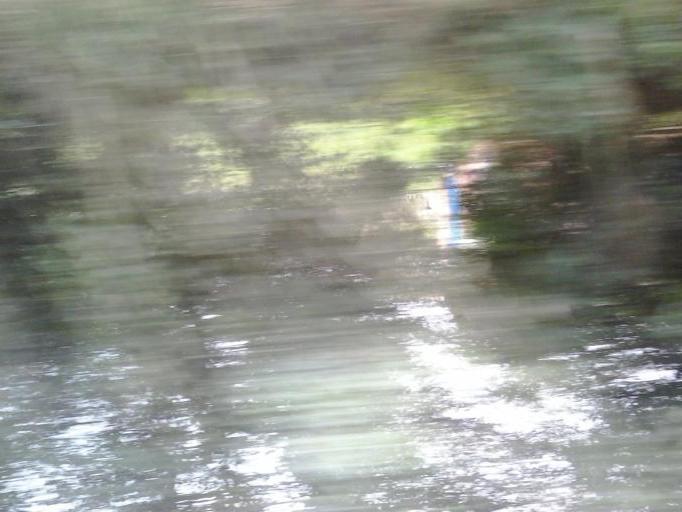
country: BR
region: Rio Grande do Sul
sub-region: Santa Maria
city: Santa Maria
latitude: -29.7225
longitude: -53.7219
